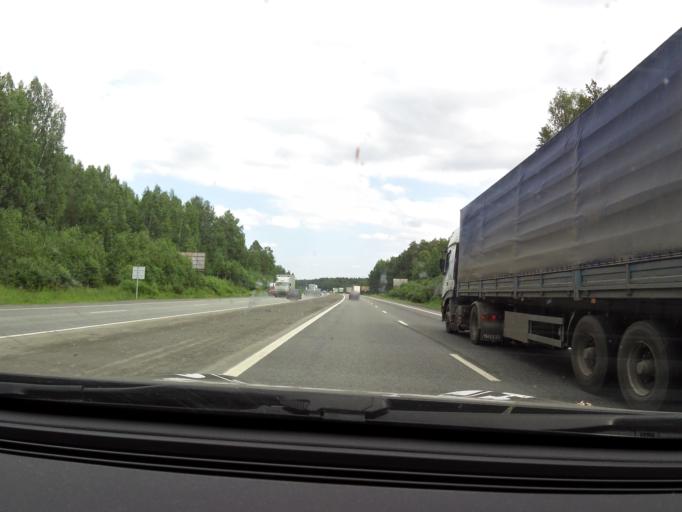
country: RU
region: Sverdlovsk
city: Talitsa
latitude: 56.8417
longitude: 60.1008
